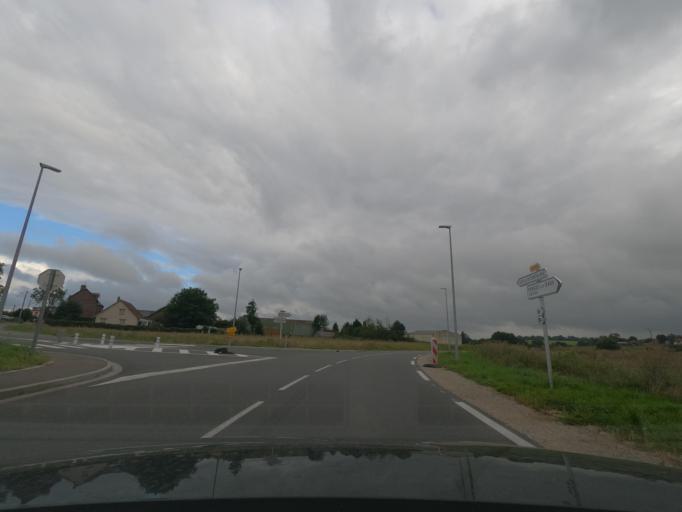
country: FR
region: Haute-Normandie
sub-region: Departement de la Seine-Maritime
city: Forges-les-Eaux
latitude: 49.6137
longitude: 1.5556
